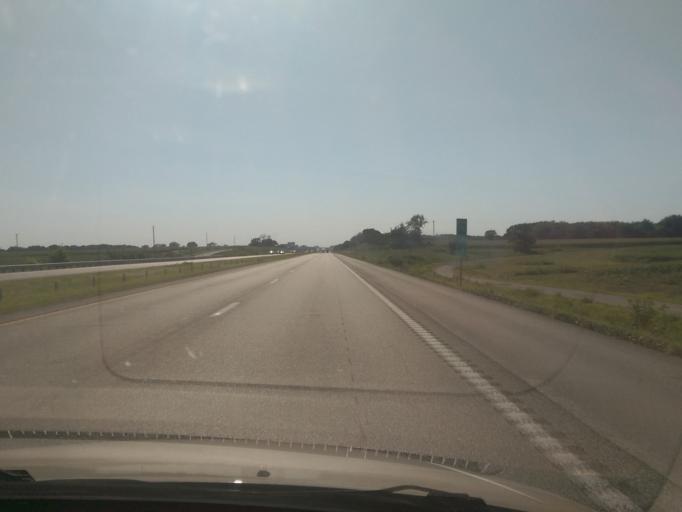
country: US
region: Missouri
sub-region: Saline County
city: Sweet Springs
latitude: 38.9722
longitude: -93.2877
